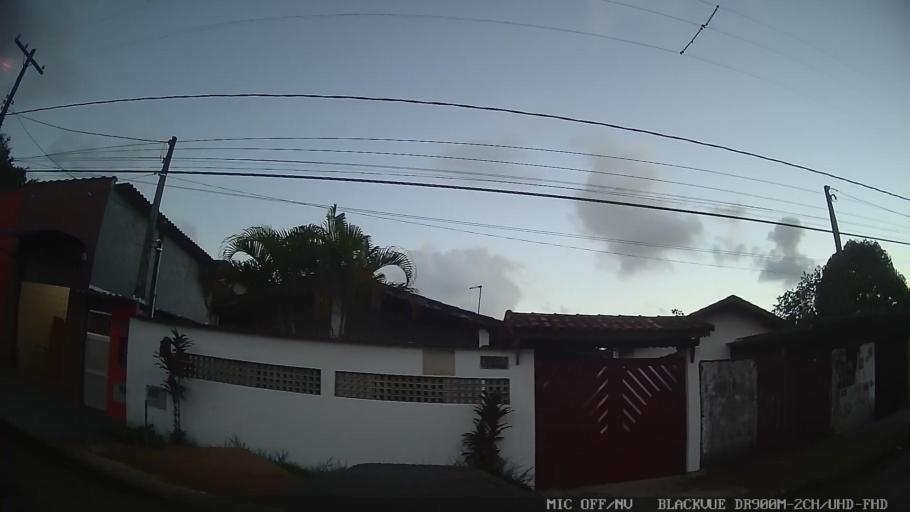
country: BR
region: Sao Paulo
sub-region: Itanhaem
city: Itanhaem
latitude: -24.1472
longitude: -46.7393
